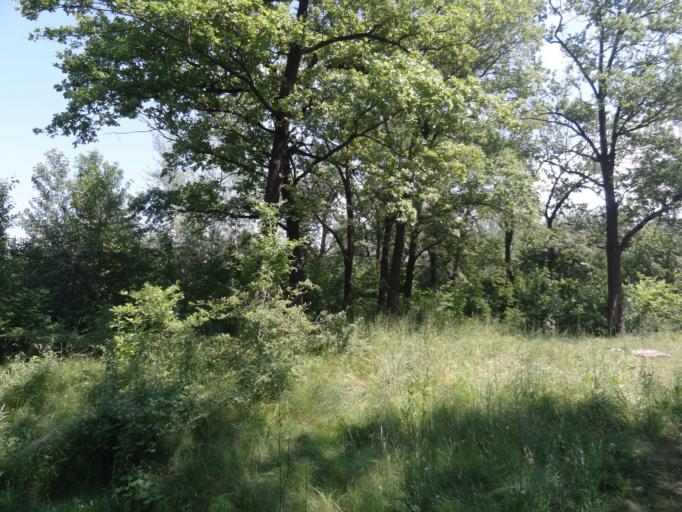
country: RU
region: Saratov
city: Engel's
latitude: 51.5481
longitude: 46.1217
